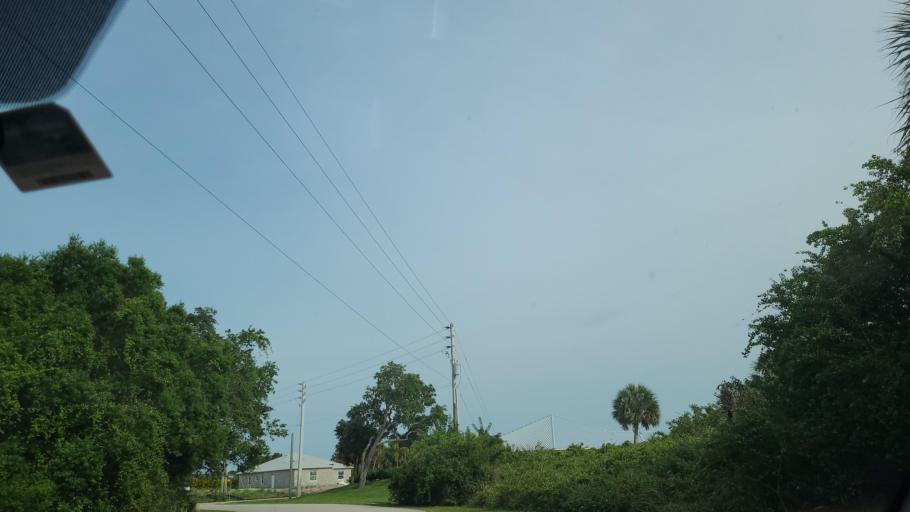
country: US
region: Florida
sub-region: Indian River County
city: Sebastian
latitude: 27.7887
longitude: -80.4784
